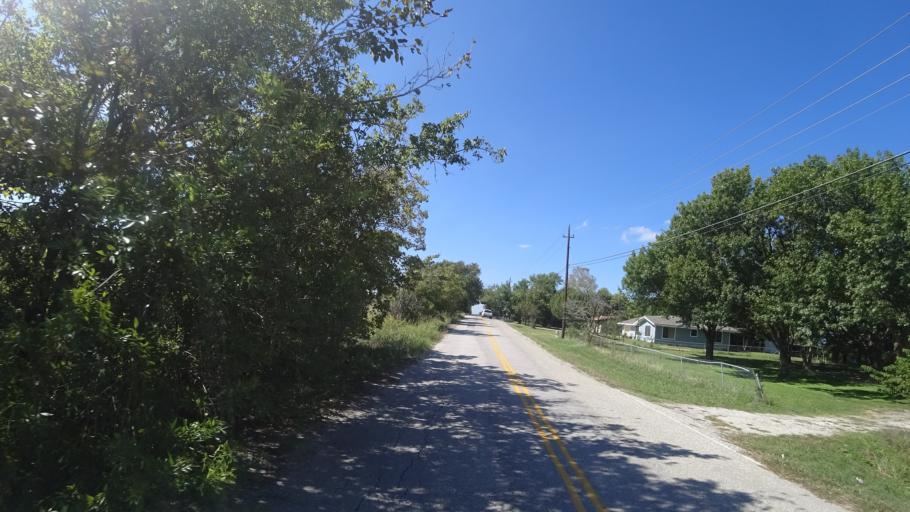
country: US
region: Texas
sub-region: Travis County
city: Manor
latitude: 30.3386
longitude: -97.6056
